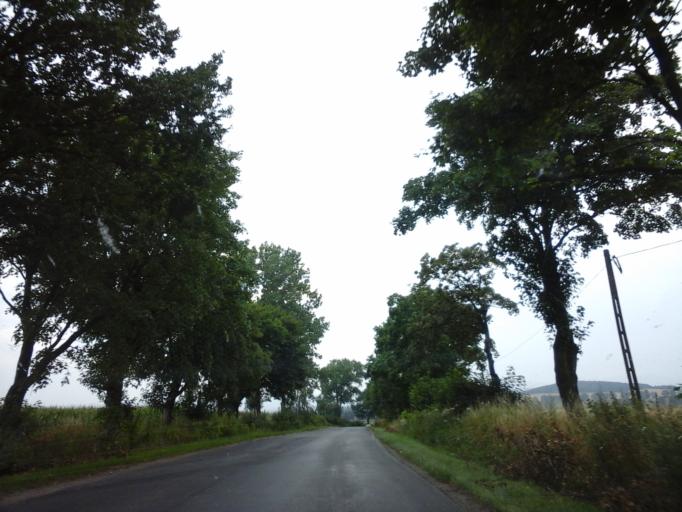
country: PL
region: Lower Silesian Voivodeship
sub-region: Powiat zabkowicki
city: Cieplowody
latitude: 50.6275
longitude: 16.8719
